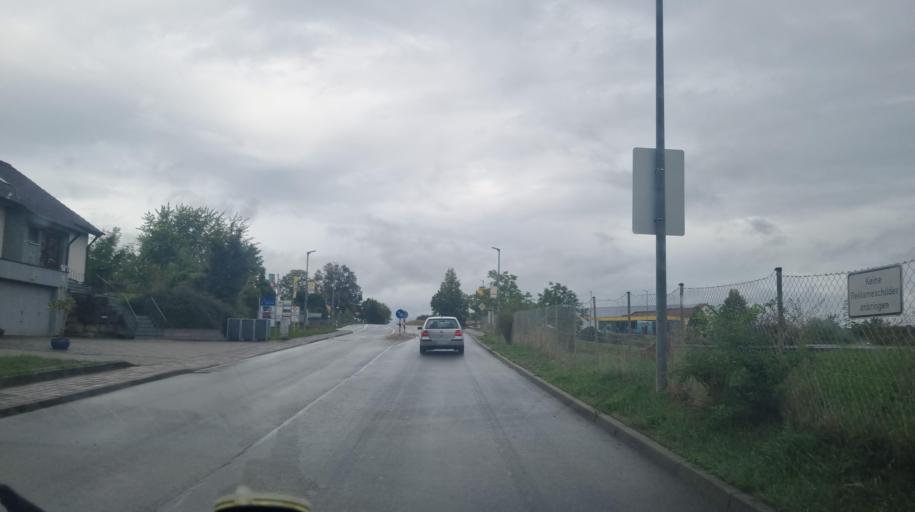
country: DE
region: Baden-Wuerttemberg
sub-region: Regierungsbezirk Stuttgart
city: Motzingen
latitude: 48.5367
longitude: 8.7717
